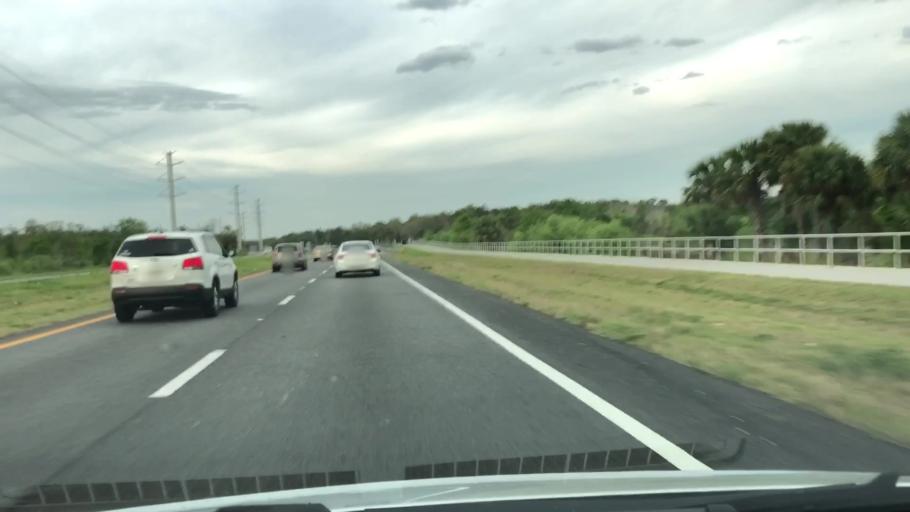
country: US
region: Florida
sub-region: Seminole County
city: Midway
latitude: 28.8143
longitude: -81.1925
